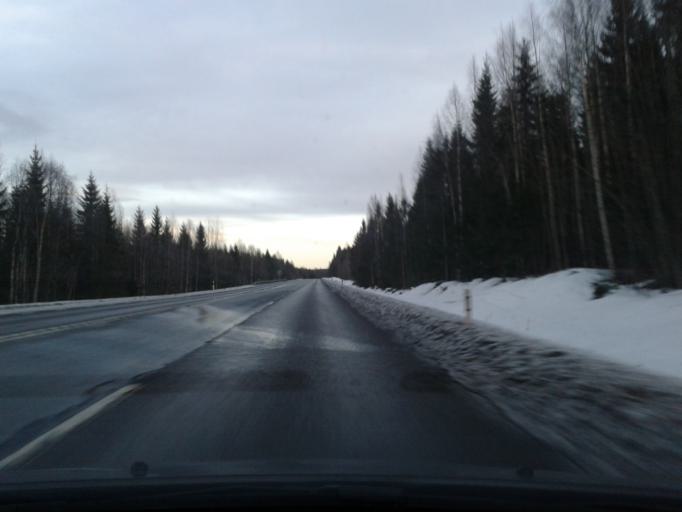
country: SE
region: Vaesternorrland
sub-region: Solleftea Kommun
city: Solleftea
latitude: 63.1419
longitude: 17.4172
